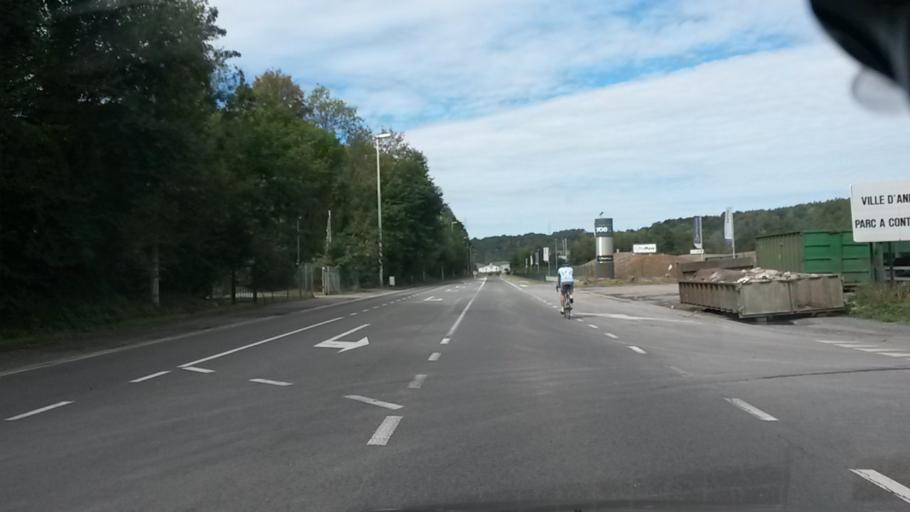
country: BE
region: Wallonia
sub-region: Province de Namur
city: Andenne
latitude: 50.4939
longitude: 5.0575
